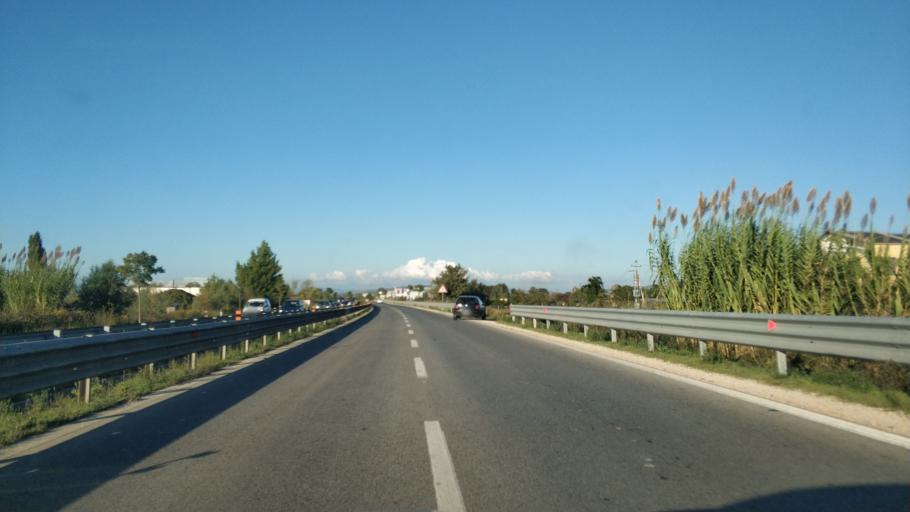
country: AL
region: Fier
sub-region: Rrethi i Lushnjes
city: Krutja e Poshtme
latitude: 40.8610
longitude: 19.6497
